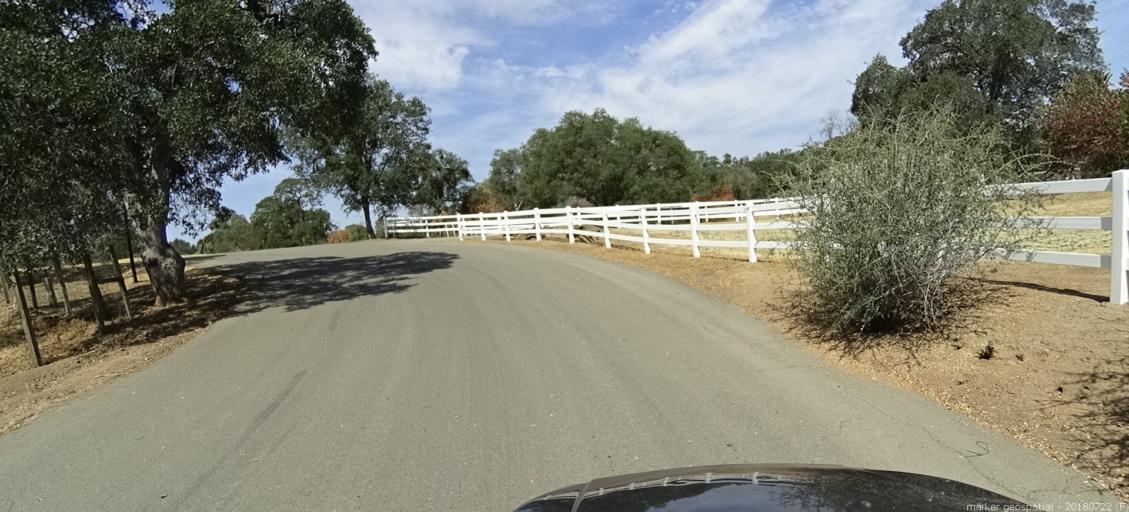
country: US
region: California
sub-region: Madera County
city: Coarsegold
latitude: 37.2584
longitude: -119.7128
